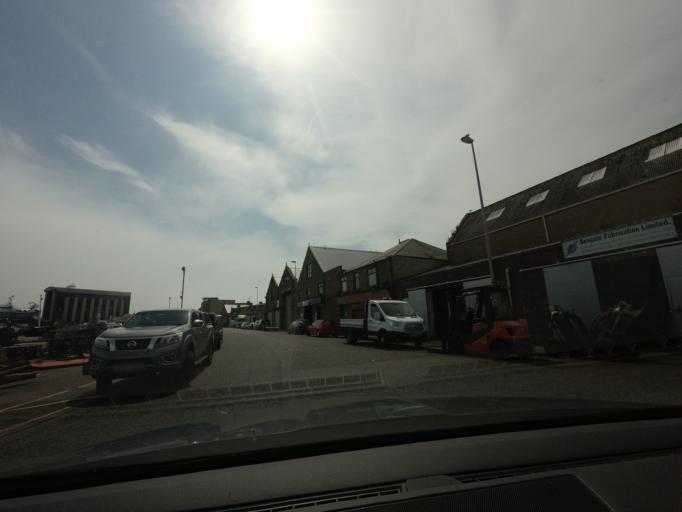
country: GB
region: Scotland
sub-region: Aberdeenshire
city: Peterhead
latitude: 57.5066
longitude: -1.7757
